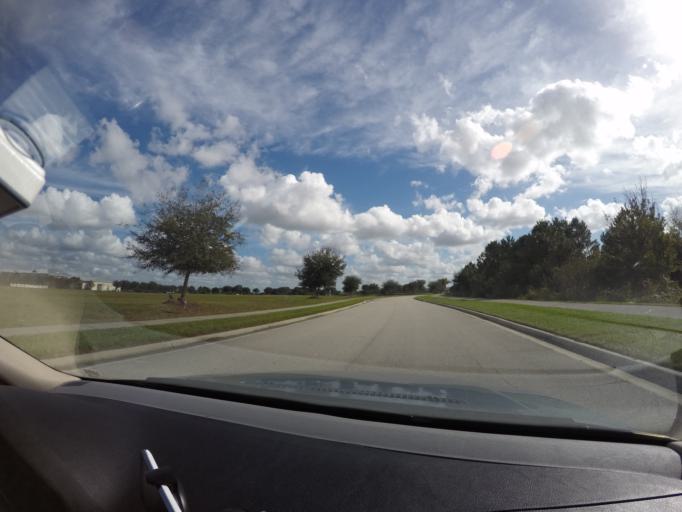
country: US
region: Florida
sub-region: Orange County
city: Wedgefield
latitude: 28.4122
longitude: -81.2055
